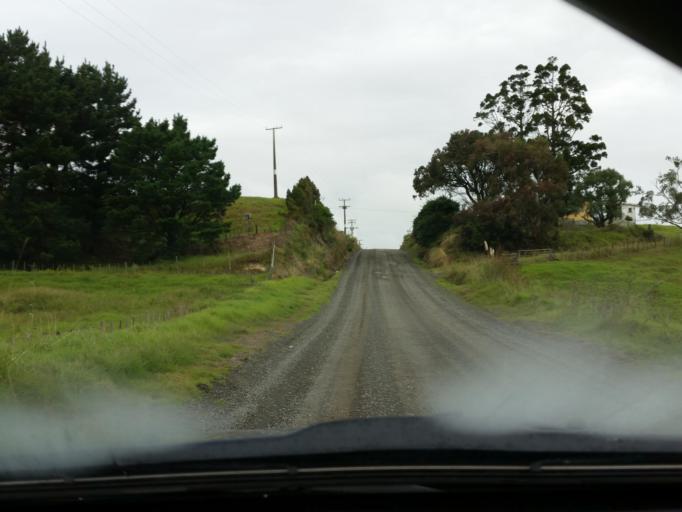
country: NZ
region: Northland
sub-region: Kaipara District
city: Dargaville
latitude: -36.0125
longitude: 173.8916
